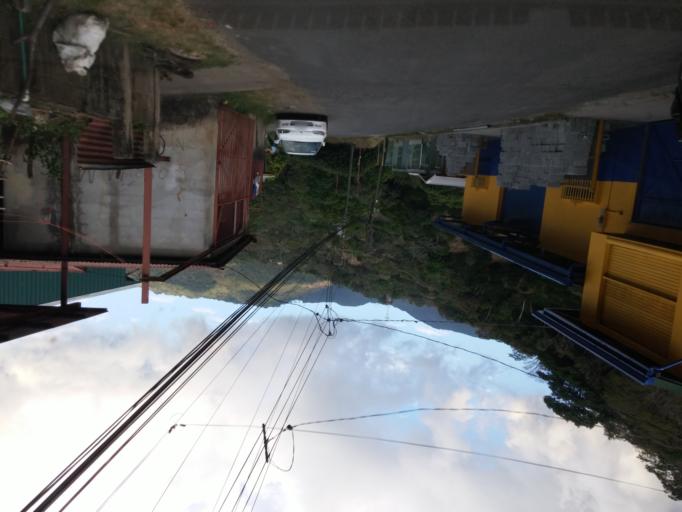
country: CR
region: San Jose
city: San Ignacio
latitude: 9.8087
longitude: -84.1801
